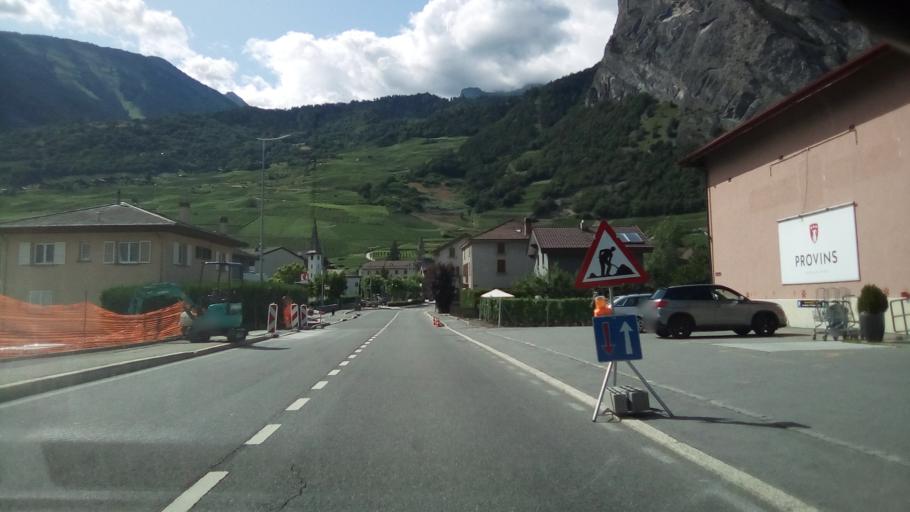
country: CH
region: Valais
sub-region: Martigny District
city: Leytron
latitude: 46.1853
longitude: 7.2105
